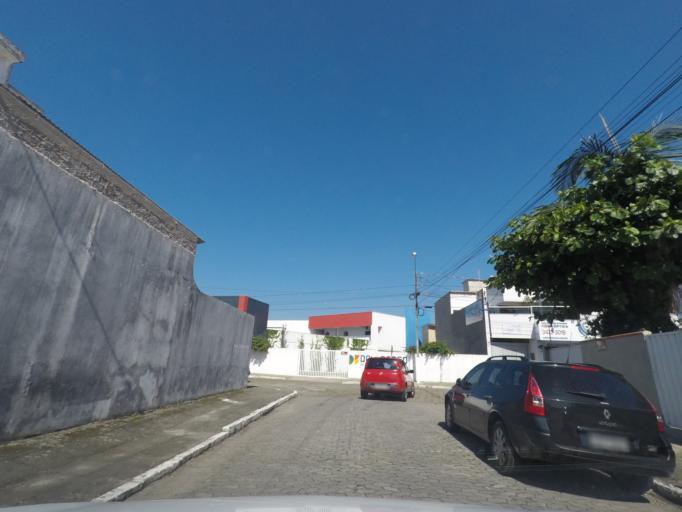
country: BR
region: Parana
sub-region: Guaratuba
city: Guaratuba
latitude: -25.8182
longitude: -48.5363
